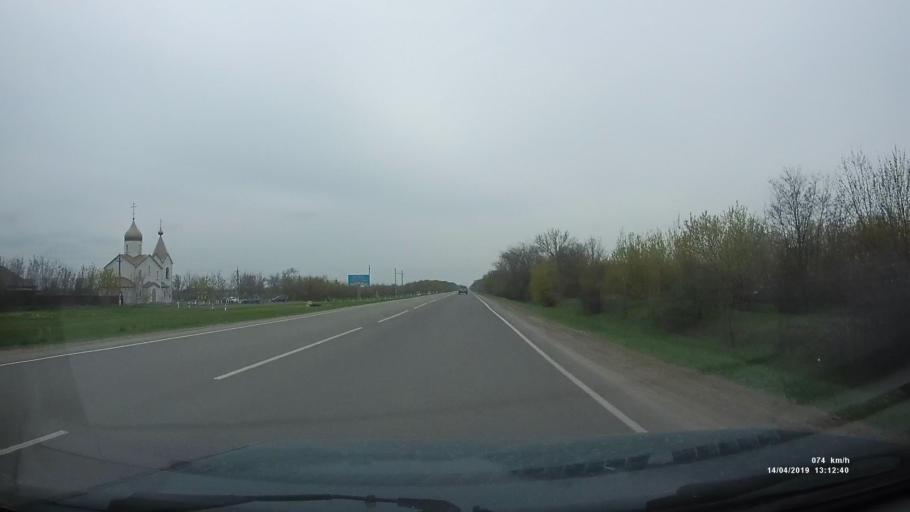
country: RU
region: Rostov
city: Kuleshovka
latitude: 47.1016
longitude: 39.6349
